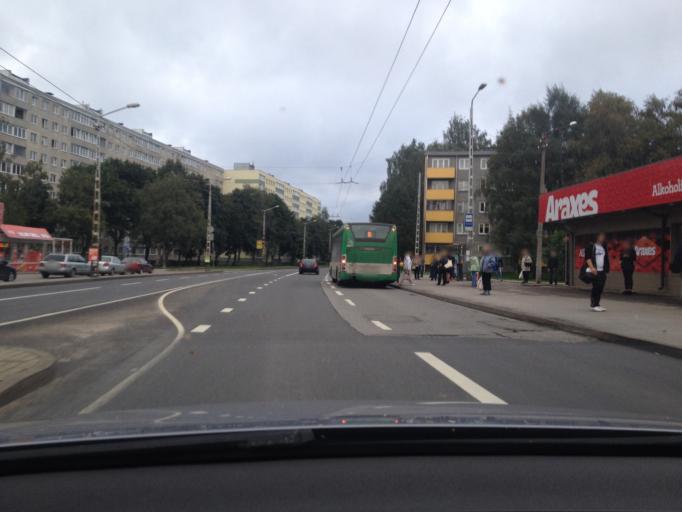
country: EE
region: Harju
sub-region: Saue vald
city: Laagri
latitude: 59.4049
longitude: 24.6761
